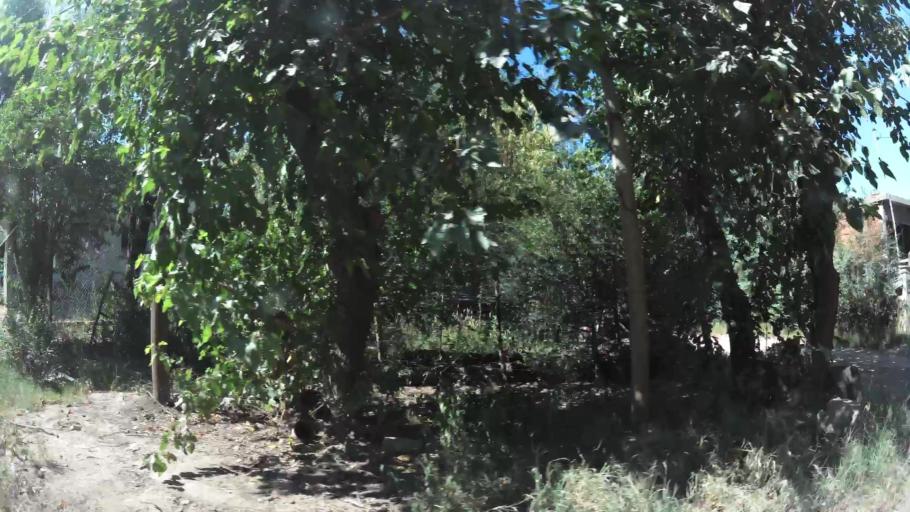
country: AR
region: Cordoba
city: Mendiolaza
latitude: -31.2703
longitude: -64.2981
